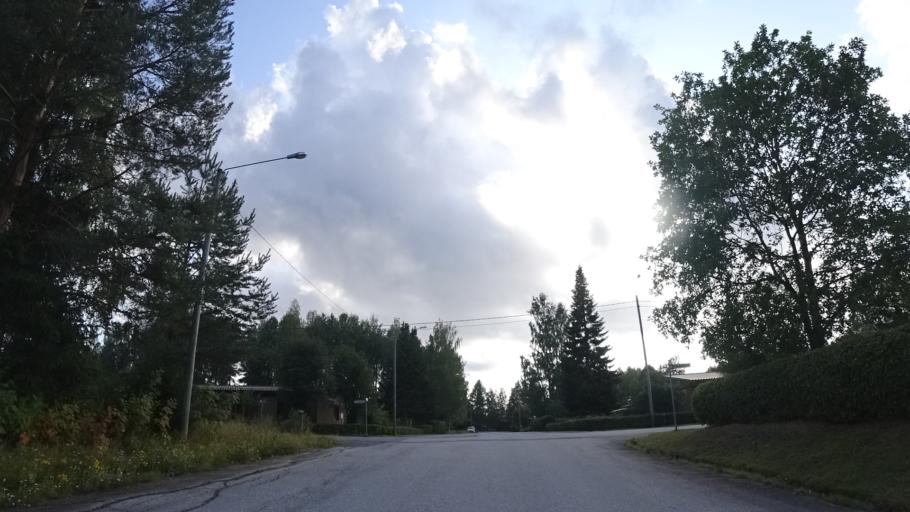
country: FI
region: North Karelia
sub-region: Pielisen Karjala
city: Lieksa
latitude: 63.3336
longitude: 30.0334
